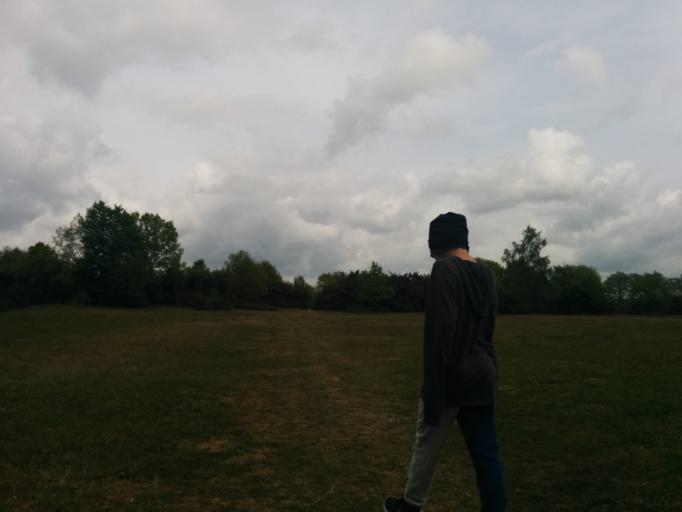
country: SE
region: Skane
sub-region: Lunds Kommun
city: Genarp
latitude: 55.5876
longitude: 13.3964
